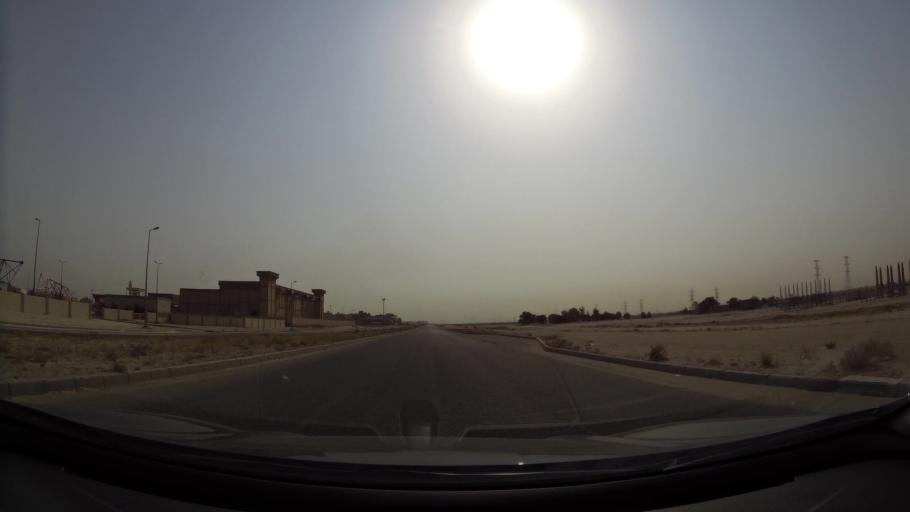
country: KW
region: Muhafazat al Jahra'
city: Al Jahra'
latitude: 29.3443
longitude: 47.7350
